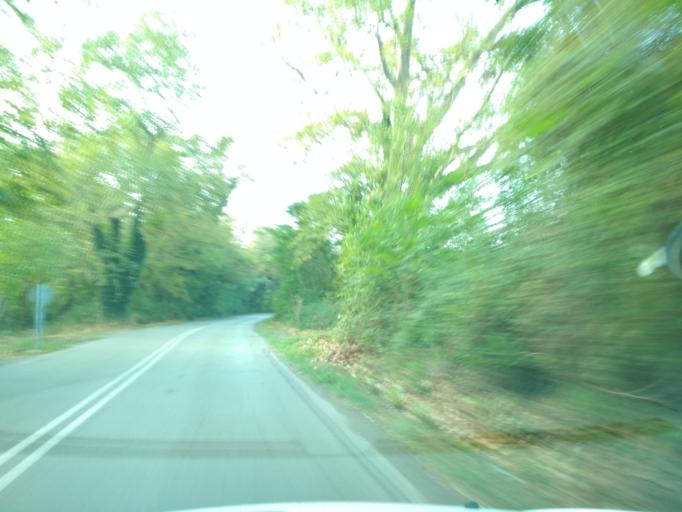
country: GR
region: Central Greece
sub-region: Nomos Evvoias
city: Prokopion
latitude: 38.7481
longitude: 23.4884
